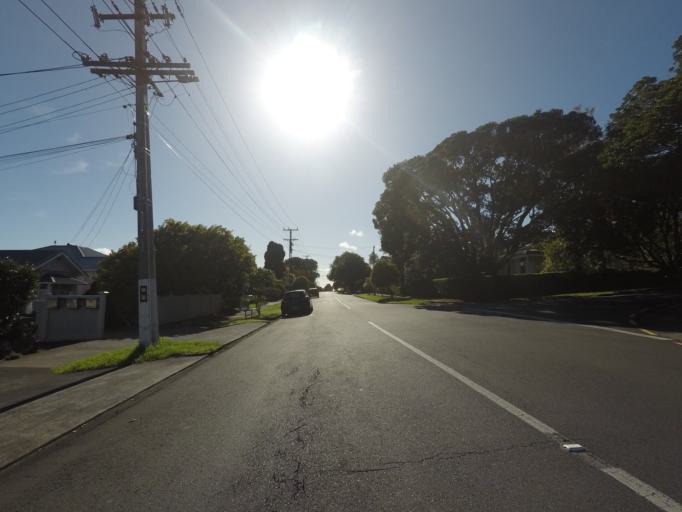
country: NZ
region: Auckland
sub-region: Auckland
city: Rosebank
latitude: -36.8870
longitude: 174.7157
